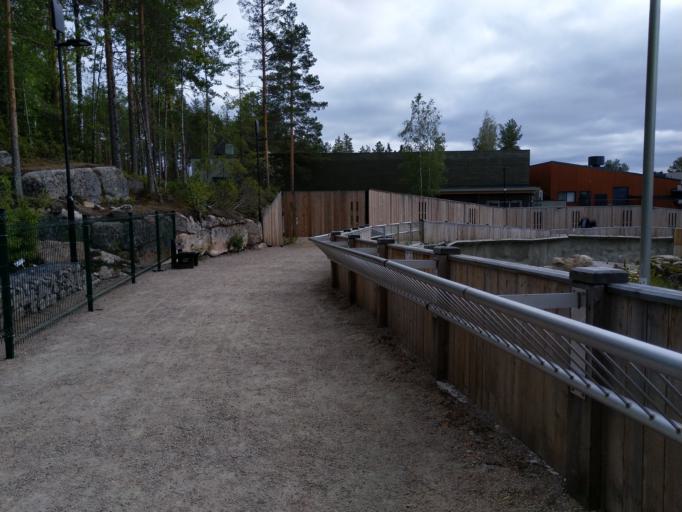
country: FI
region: Southern Ostrobothnia
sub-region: Kuusiokunnat
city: AEhtaeri
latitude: 62.5373
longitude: 24.1844
